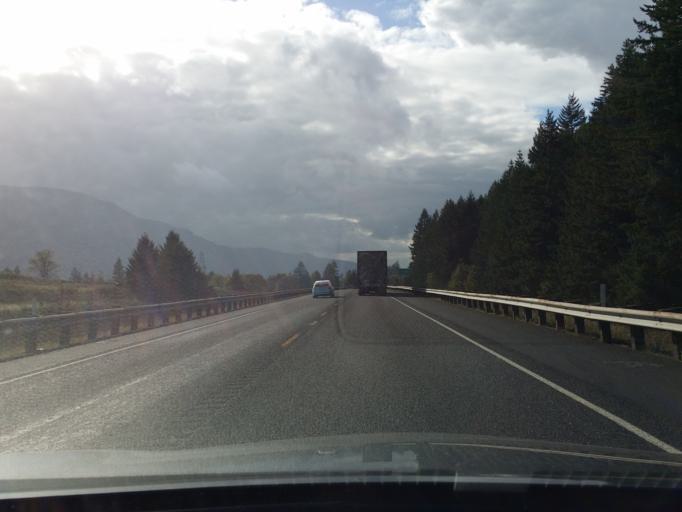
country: US
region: Oregon
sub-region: Hood River County
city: Cascade Locks
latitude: 45.6432
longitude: -121.9638
